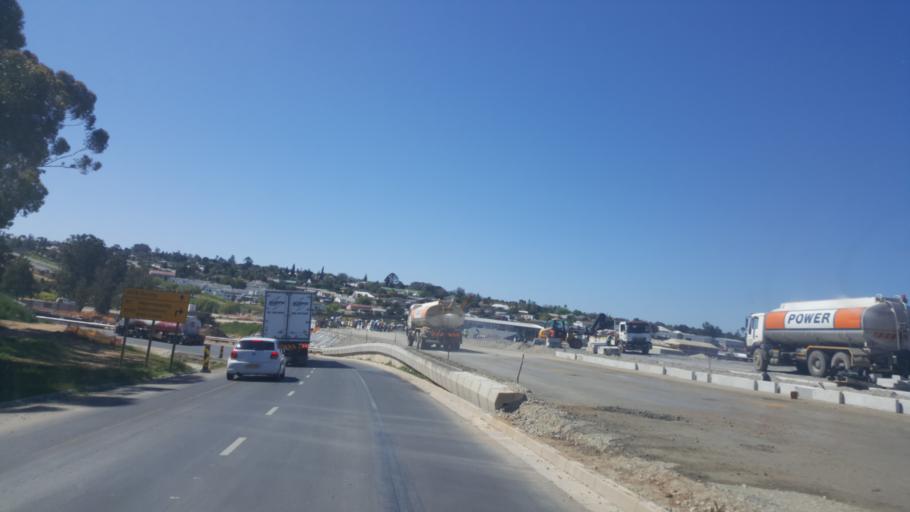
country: ZA
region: Western Cape
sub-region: West Coast District Municipality
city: Malmesbury
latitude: -33.4665
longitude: 18.7164
